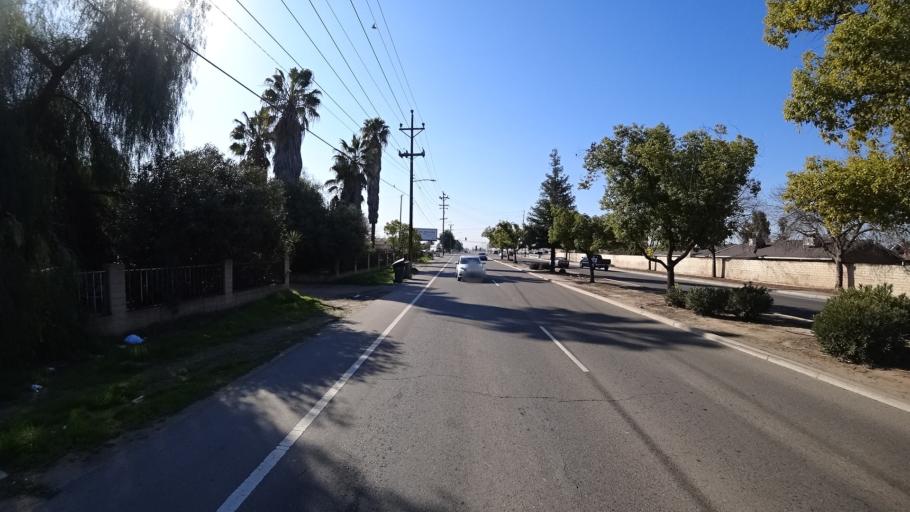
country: US
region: California
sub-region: Fresno County
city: Fresno
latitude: 36.7088
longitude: -119.7364
